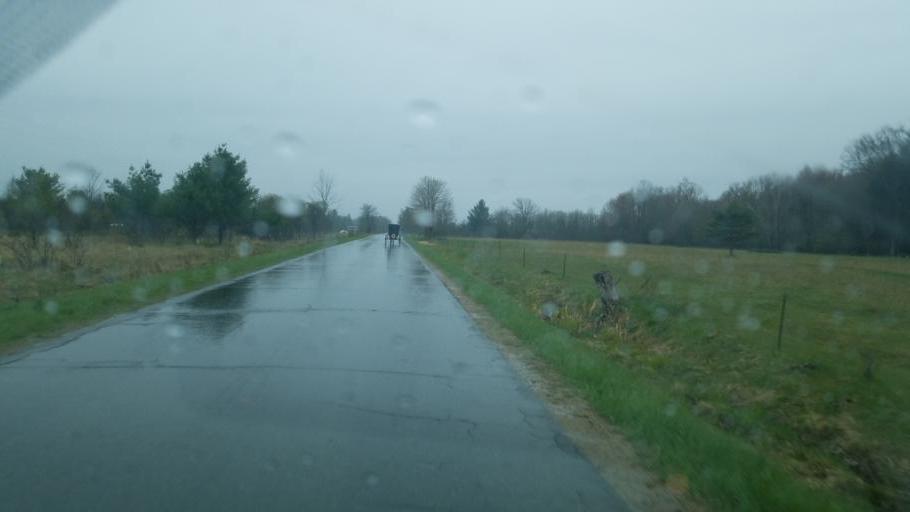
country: US
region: Michigan
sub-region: Mecosta County
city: Canadian Lakes
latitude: 43.5375
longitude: -85.2841
